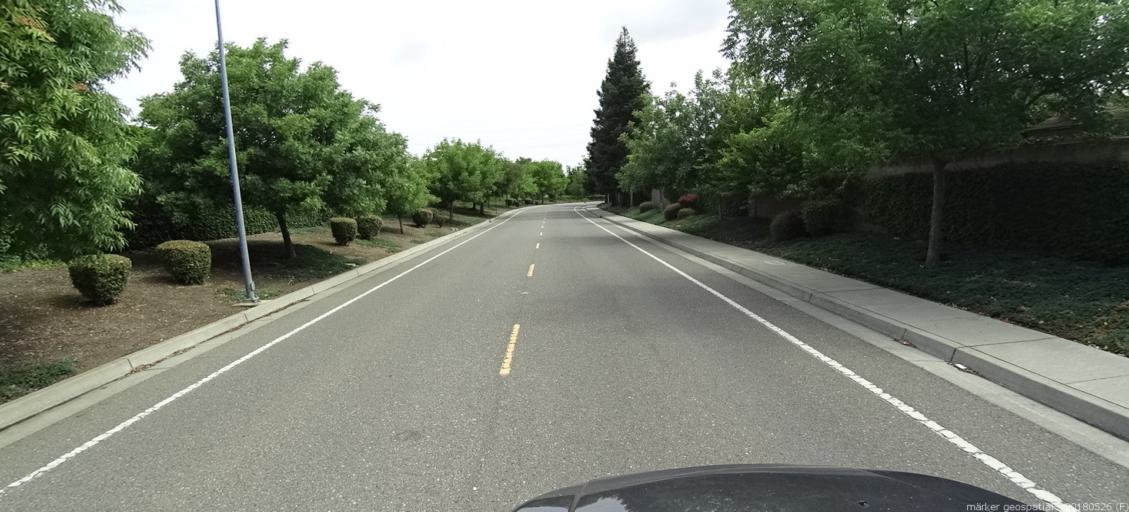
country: US
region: California
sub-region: Yolo County
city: West Sacramento
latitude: 38.6112
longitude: -121.5385
